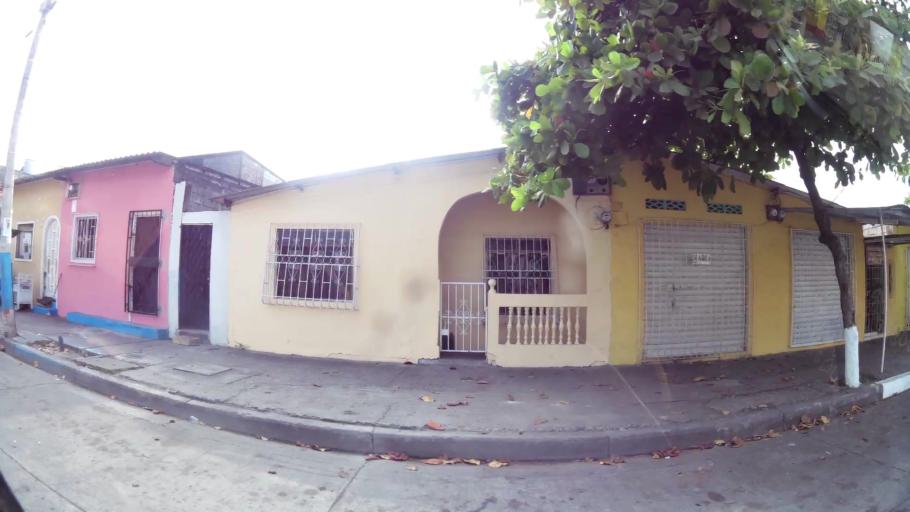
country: EC
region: Guayas
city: Guayaquil
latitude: -2.2451
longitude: -79.8883
